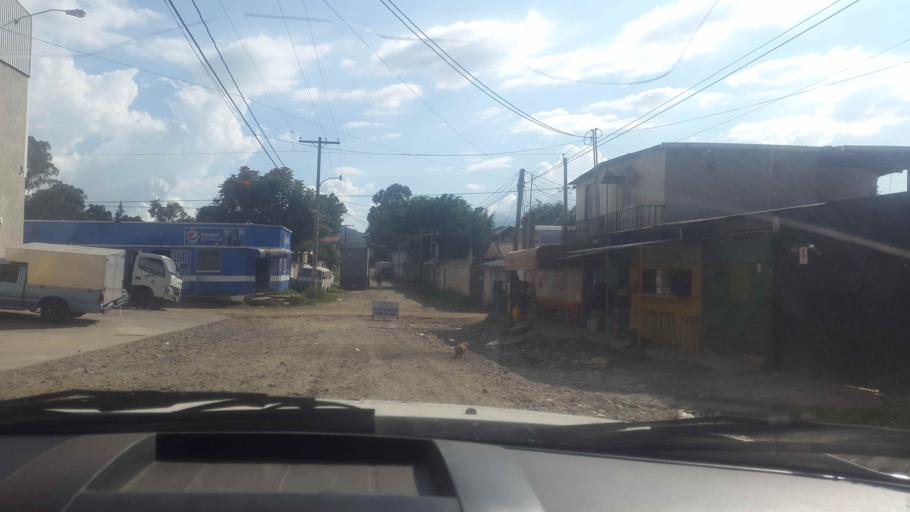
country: GT
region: Guatemala
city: Petapa
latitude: 14.5115
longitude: -90.5417
